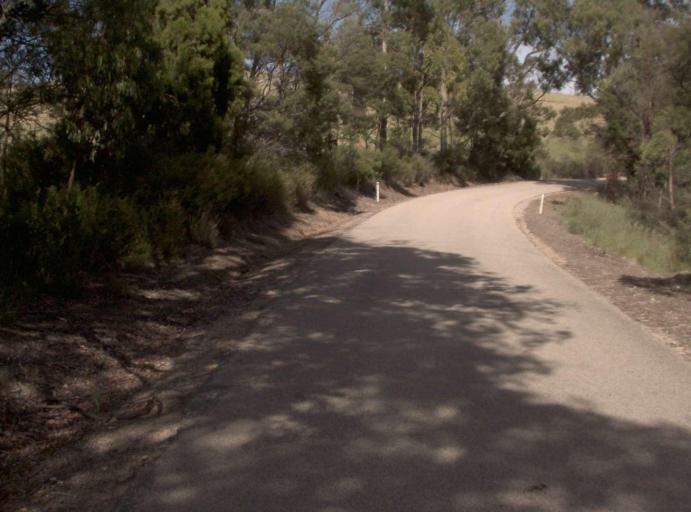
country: AU
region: Victoria
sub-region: East Gippsland
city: Lakes Entrance
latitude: -37.5246
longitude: 148.1428
